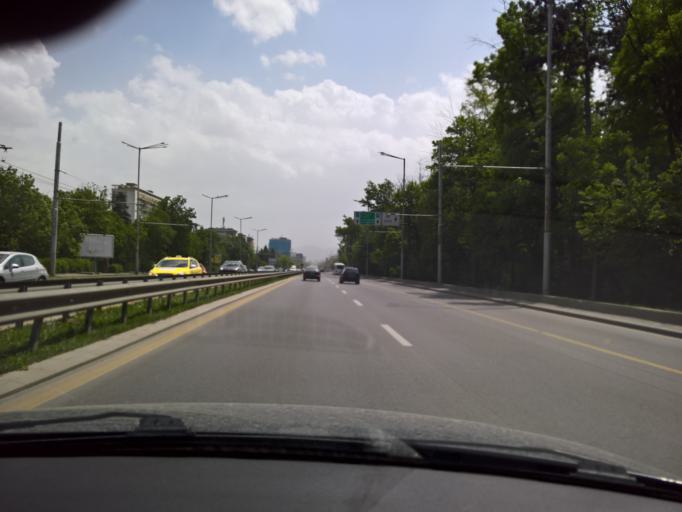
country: BG
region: Sofia-Capital
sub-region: Stolichna Obshtina
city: Sofia
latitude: 42.6789
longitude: 23.3538
